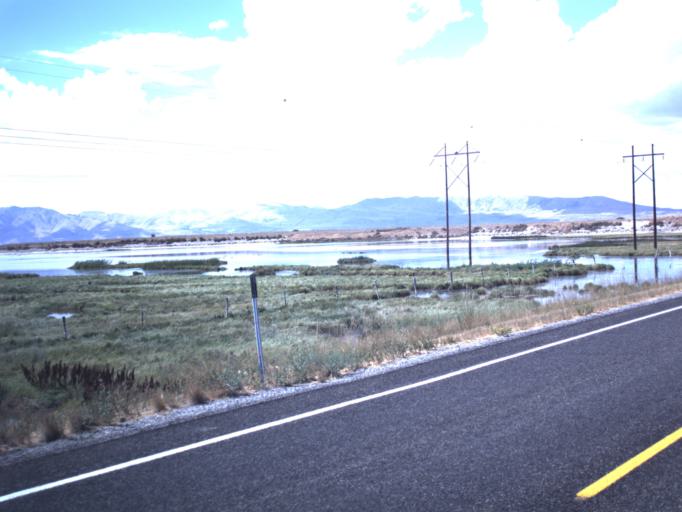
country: US
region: Utah
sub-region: Box Elder County
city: Tremonton
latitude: 41.6027
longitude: -112.3105
